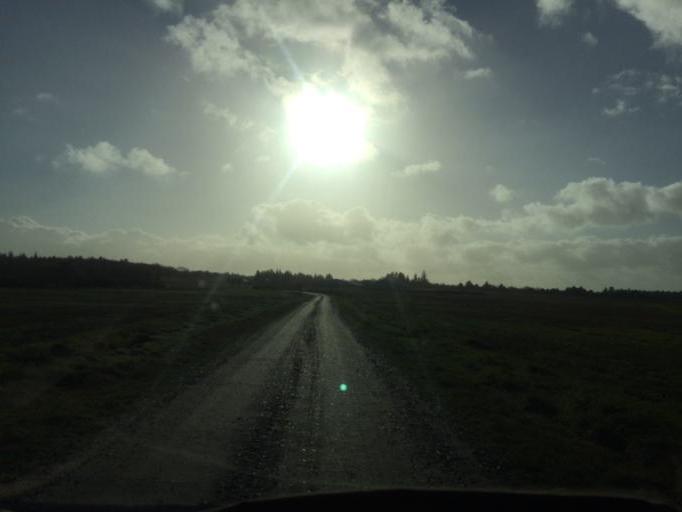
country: DK
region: Central Jutland
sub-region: Holstebro Kommune
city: Ulfborg
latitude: 56.2410
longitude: 8.4472
